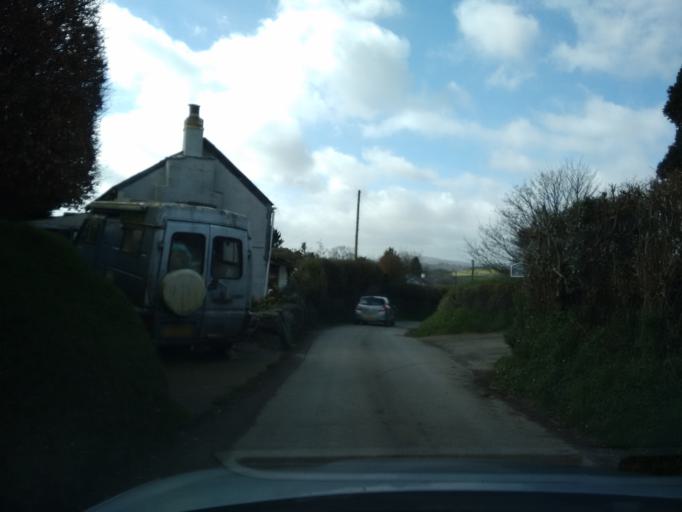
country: GB
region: England
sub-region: Cornwall
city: South Hill
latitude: 50.5803
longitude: -4.3681
